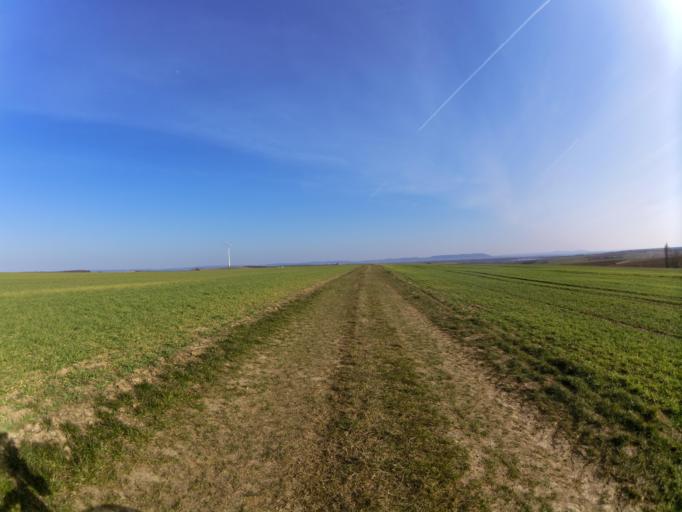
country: DE
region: Bavaria
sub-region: Regierungsbezirk Unterfranken
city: Prosselsheim
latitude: 49.8344
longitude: 10.1314
